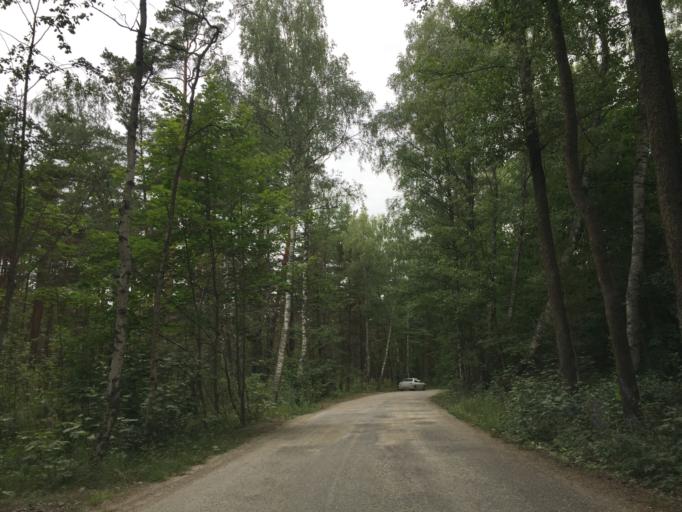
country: LV
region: Riga
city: Jaunciems
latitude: 57.0981
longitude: 24.1876
